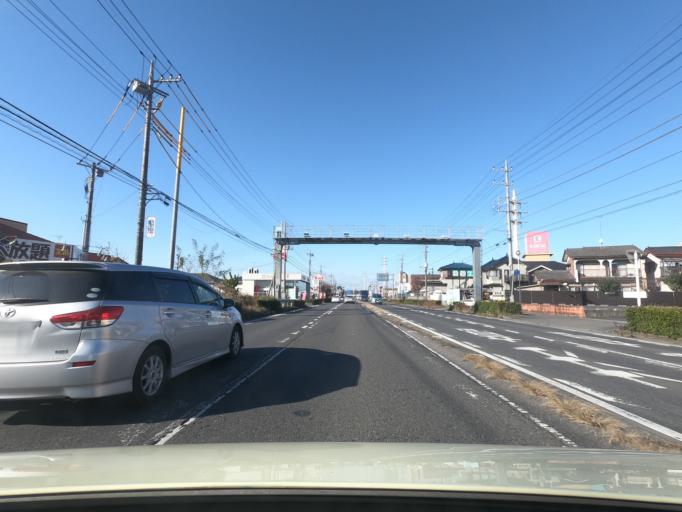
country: JP
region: Ibaraki
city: Ishige
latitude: 36.1802
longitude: 139.9523
